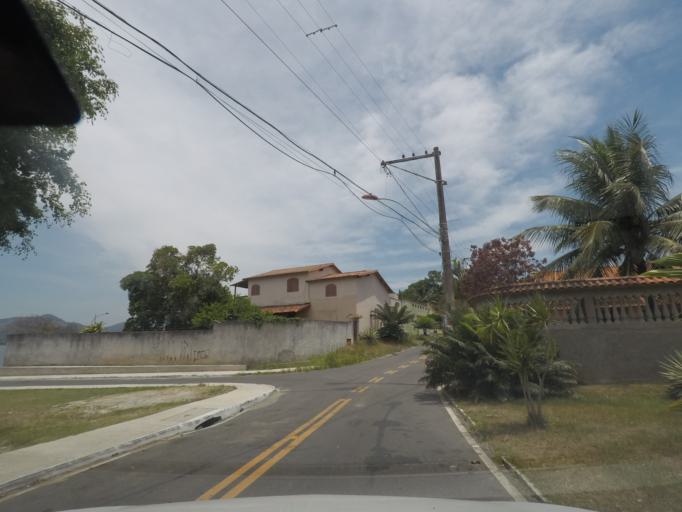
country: BR
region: Rio de Janeiro
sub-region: Marica
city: Marica
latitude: -22.9379
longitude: -42.8294
